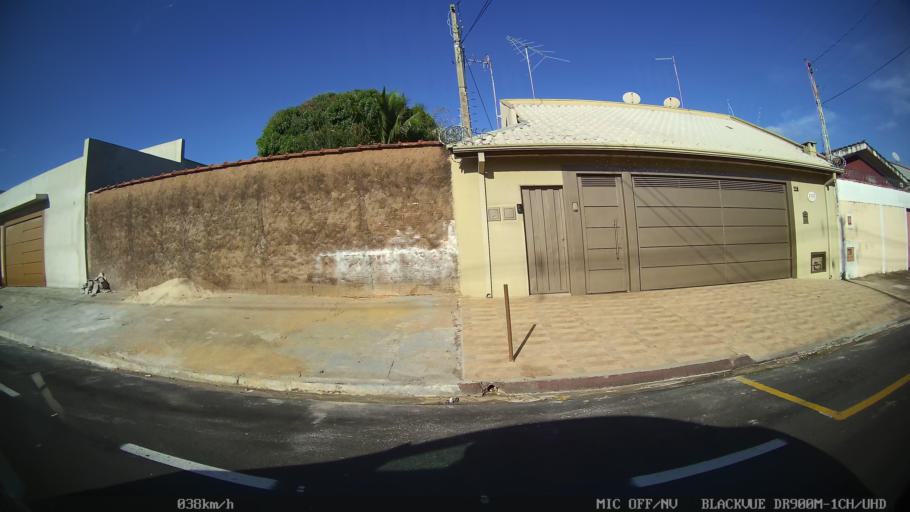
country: BR
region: Sao Paulo
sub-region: Franca
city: Franca
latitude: -20.5208
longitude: -47.4149
